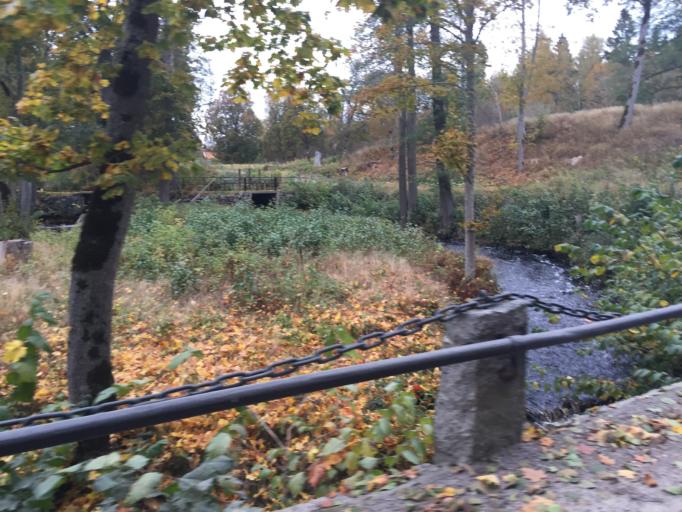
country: SE
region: OErebro
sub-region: Hallsbergs Kommun
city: Palsboda
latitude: 58.9279
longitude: 15.5207
